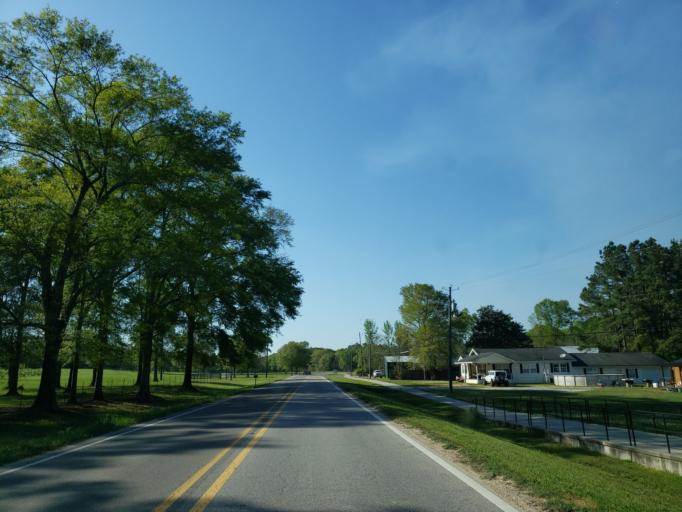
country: US
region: Mississippi
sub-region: Perry County
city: Richton
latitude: 31.3369
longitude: -88.9345
